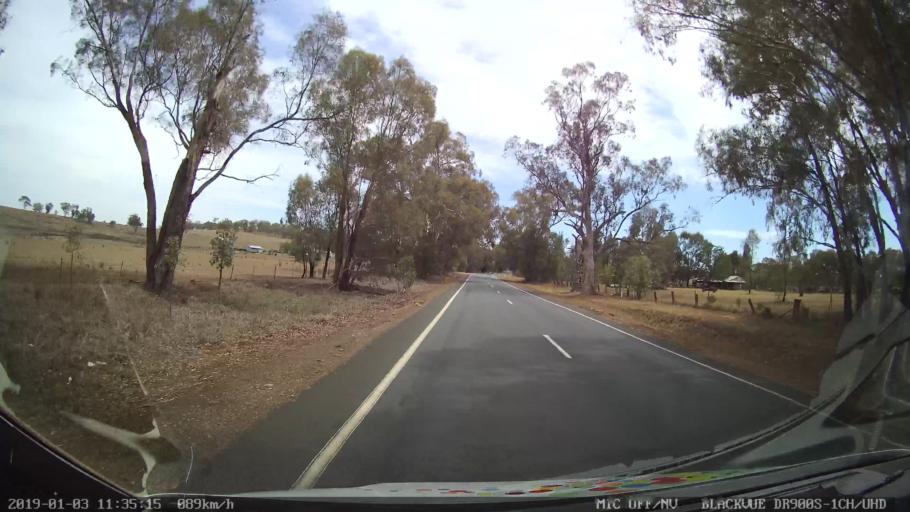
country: AU
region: New South Wales
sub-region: Weddin
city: Grenfell
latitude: -33.9246
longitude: 148.1597
